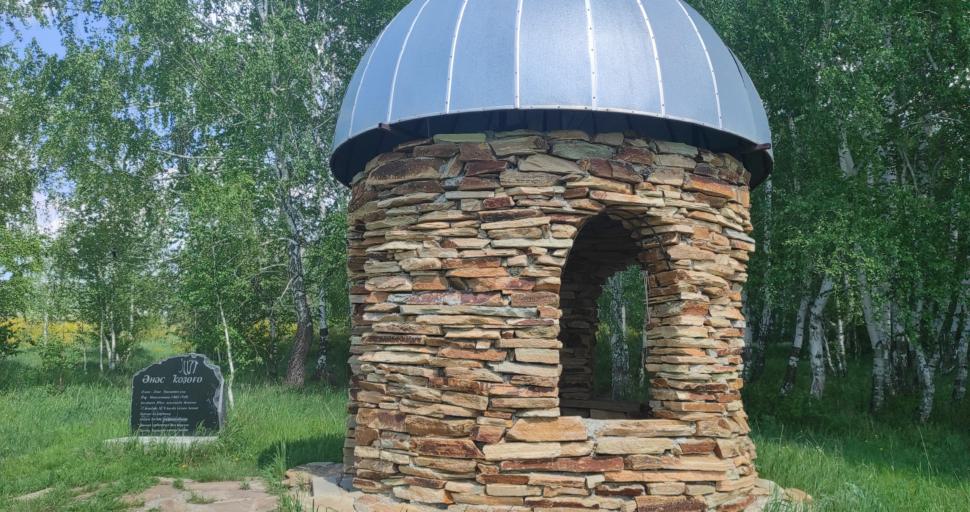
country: RU
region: Bashkortostan
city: Tubinskiy
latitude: 52.8118
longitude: 58.2477
